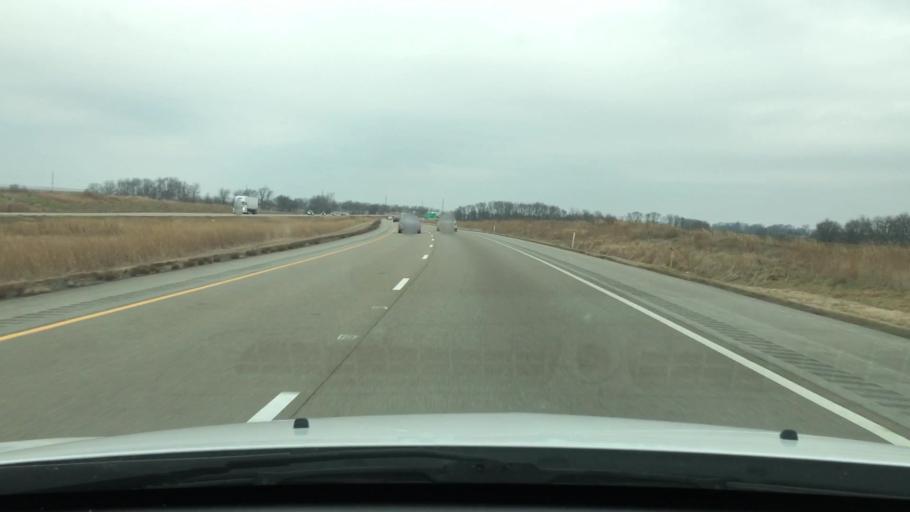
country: US
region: Illinois
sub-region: Logan County
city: Atlanta
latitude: 40.2690
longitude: -89.2129
